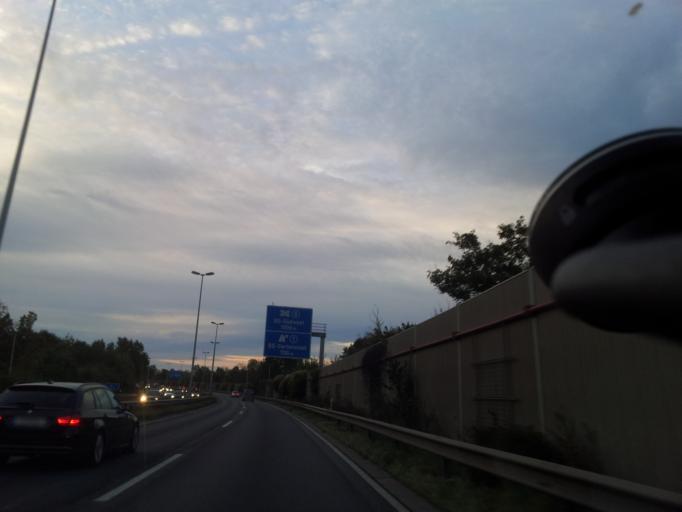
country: DE
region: Lower Saxony
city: Braunschweig
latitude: 52.2522
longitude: 10.4957
